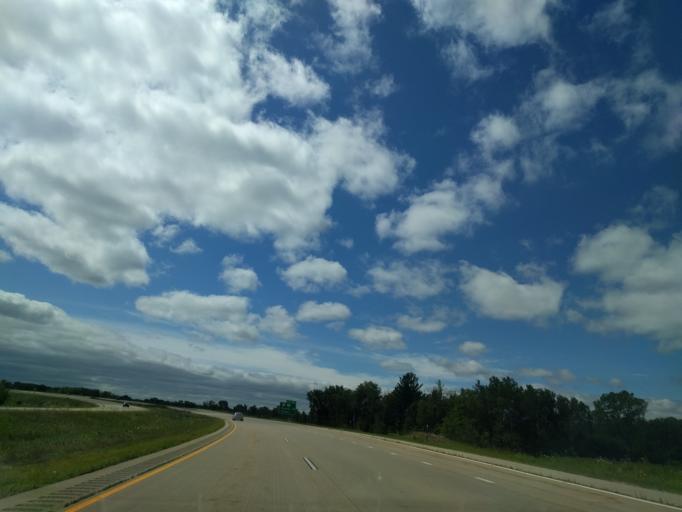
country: US
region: Wisconsin
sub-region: Oconto County
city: Oconto
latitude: 44.9001
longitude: -87.8991
